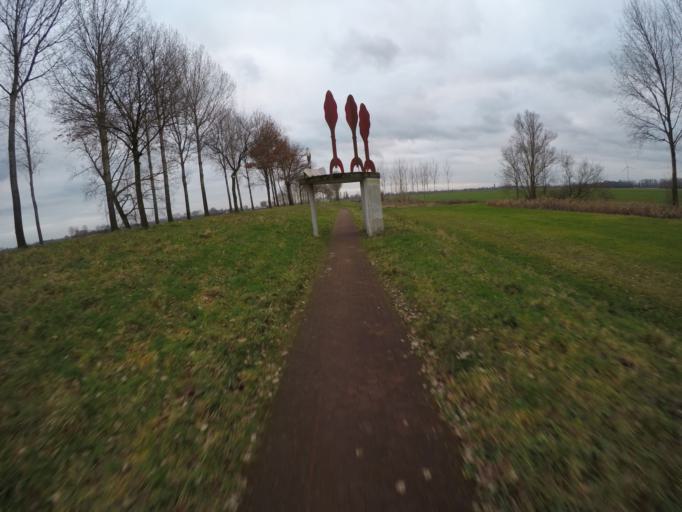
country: BE
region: Flanders
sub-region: Provincie Oost-Vlaanderen
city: Sint-Gillis-Waas
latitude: 51.2393
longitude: 4.1464
